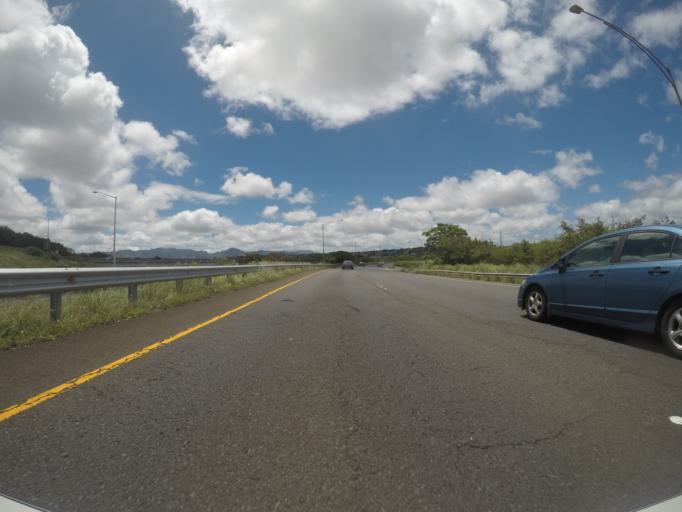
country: US
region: Hawaii
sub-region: Honolulu County
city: Pearl City, Manana
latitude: 21.3975
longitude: -157.9860
